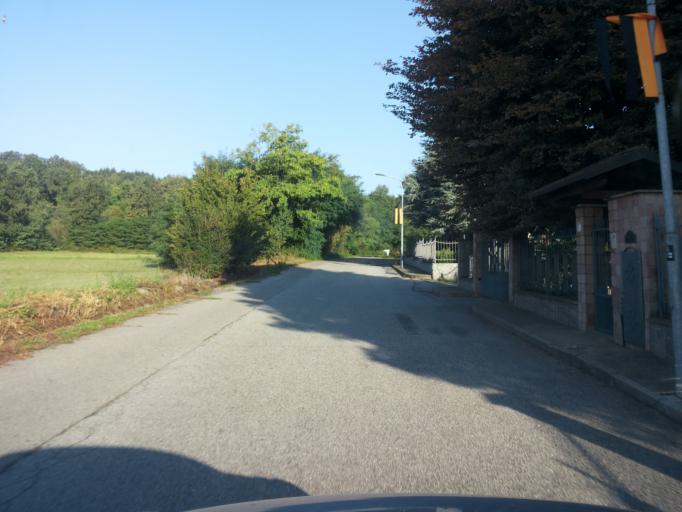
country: IT
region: Piedmont
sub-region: Provincia di Biella
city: Cavaglia
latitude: 45.4032
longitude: 8.0834
